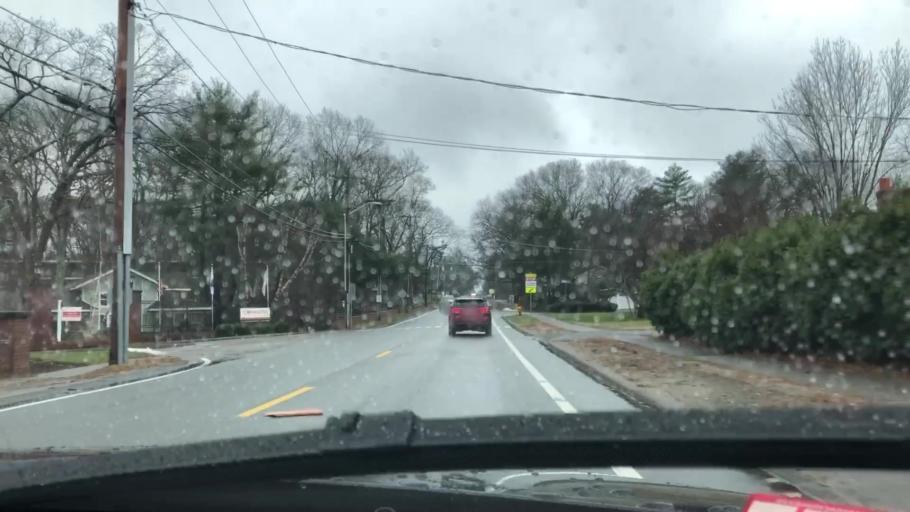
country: US
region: Massachusetts
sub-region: Norfolk County
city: Norwood
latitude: 42.1740
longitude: -71.2246
